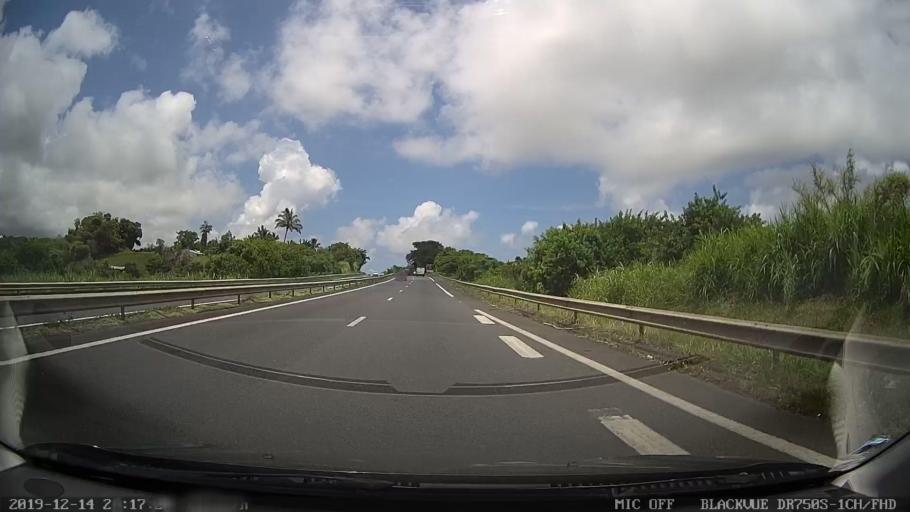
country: RE
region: Reunion
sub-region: Reunion
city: Saint-Andre
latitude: -20.9404
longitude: 55.6442
